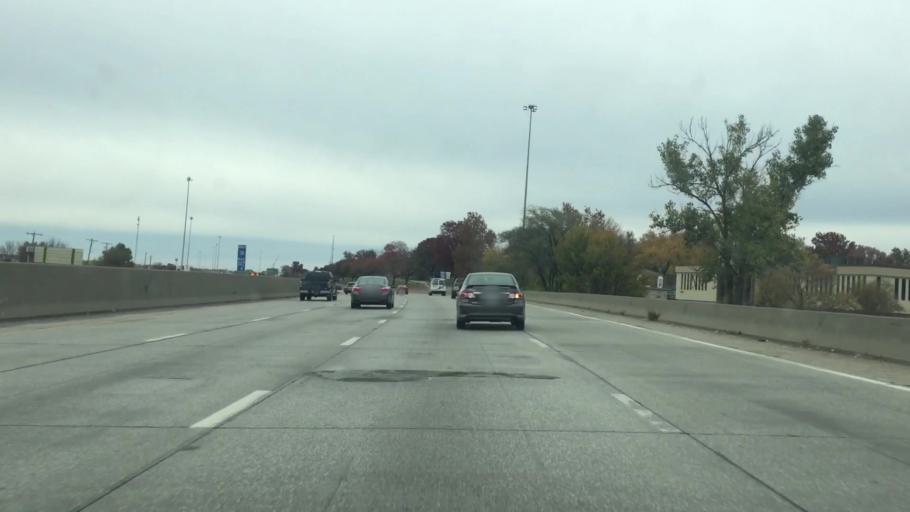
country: US
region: Kansas
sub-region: Johnson County
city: Merriam
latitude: 38.9961
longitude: -94.6956
